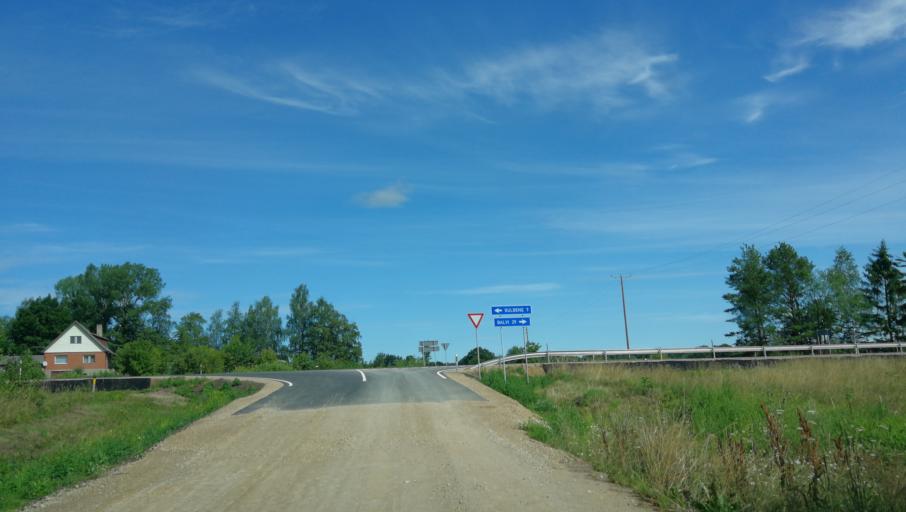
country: LV
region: Gulbenes Rajons
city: Gulbene
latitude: 57.1854
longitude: 26.8615
